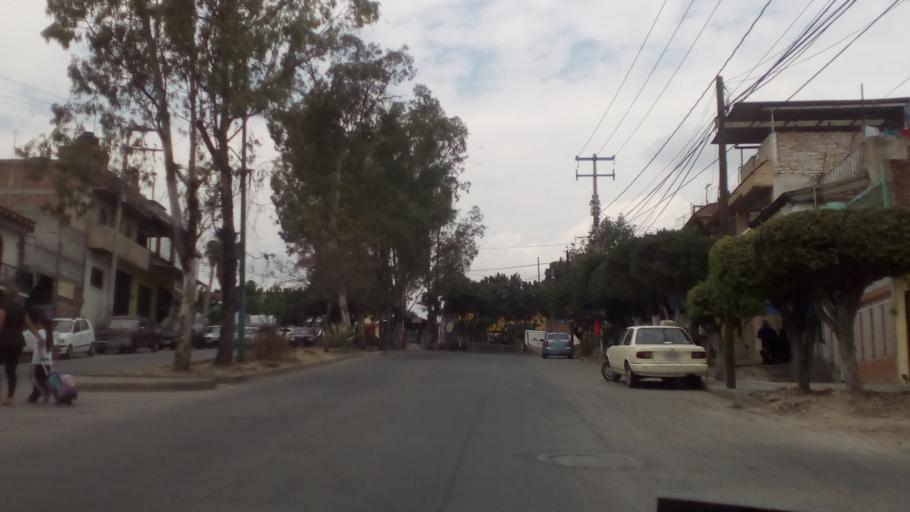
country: MX
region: Guanajuato
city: Leon
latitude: 21.1276
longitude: -101.7034
